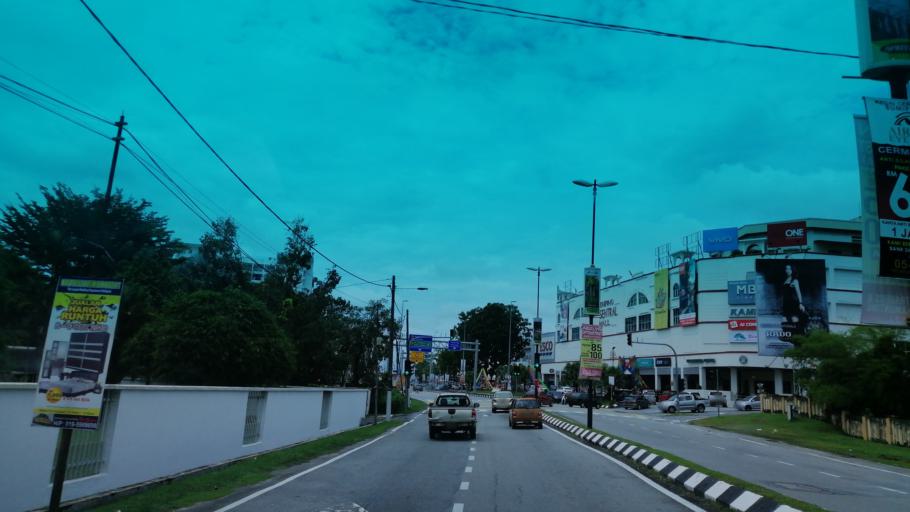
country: MY
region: Perak
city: Taiping
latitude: 4.8646
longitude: 100.7320
